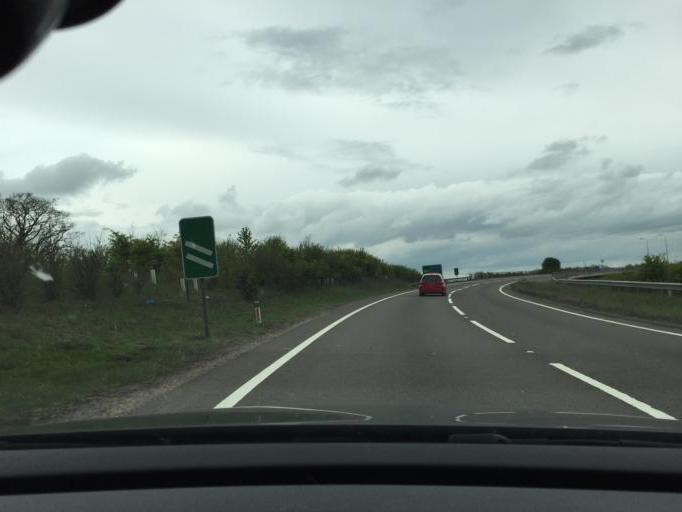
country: GB
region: England
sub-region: West Berkshire
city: Winterbourne
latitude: 51.4480
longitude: -1.3154
